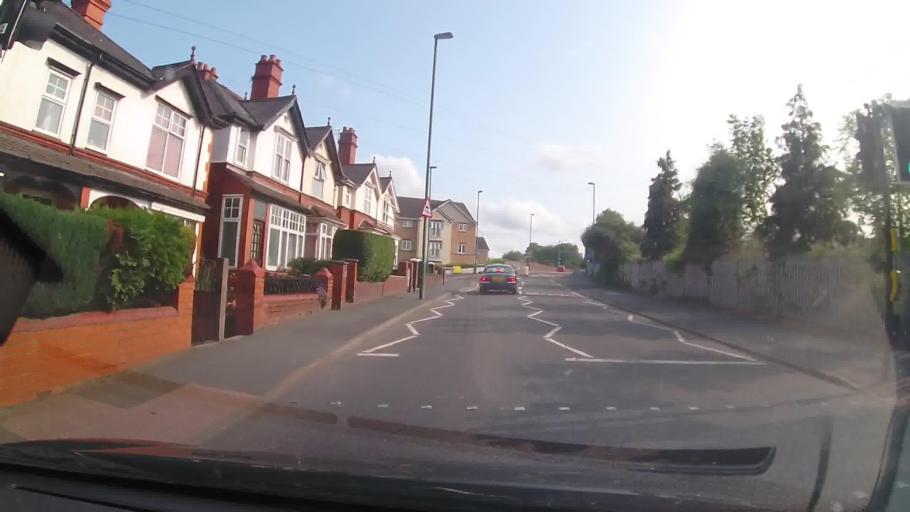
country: GB
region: England
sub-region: Shropshire
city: Shrewsbury
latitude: 52.7183
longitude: -2.7517
